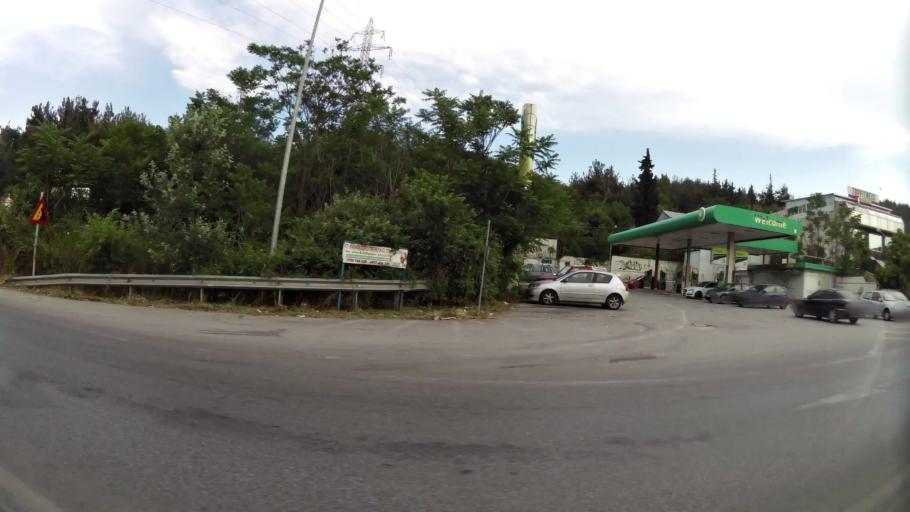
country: GR
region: Central Macedonia
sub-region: Nomos Thessalonikis
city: Pefka
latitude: 40.6592
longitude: 22.9752
